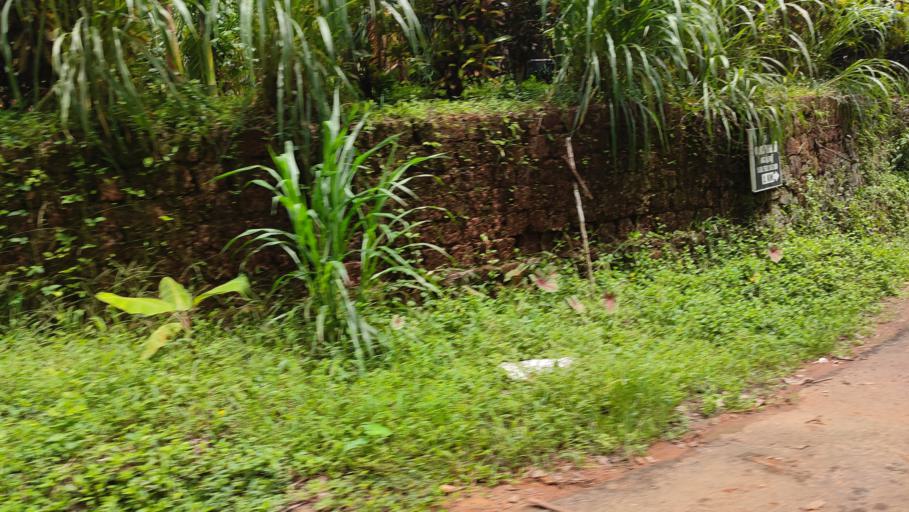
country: IN
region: Kerala
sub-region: Kasaragod District
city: Nileshwar
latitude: 12.2953
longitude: 75.2854
